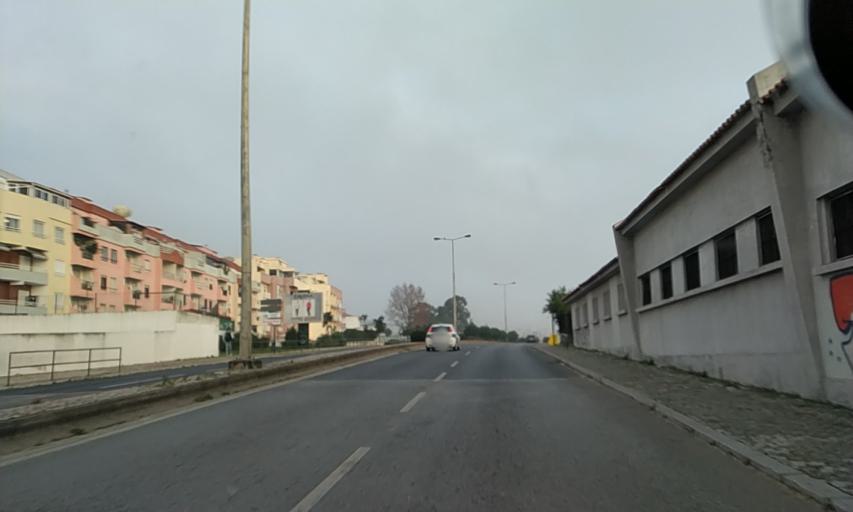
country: PT
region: Setubal
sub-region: Setubal
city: Setubal
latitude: 38.5331
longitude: -8.8754
